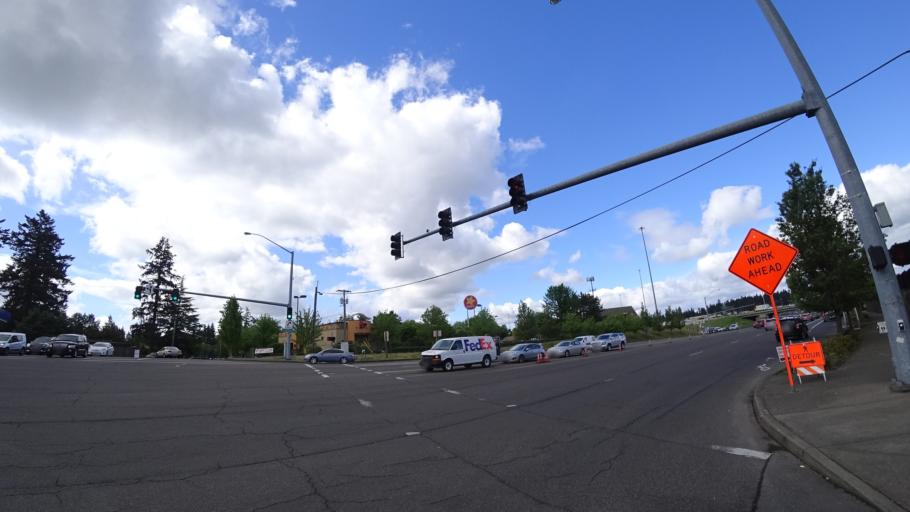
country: US
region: Oregon
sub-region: Washington County
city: Durham
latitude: 45.3967
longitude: -122.7439
